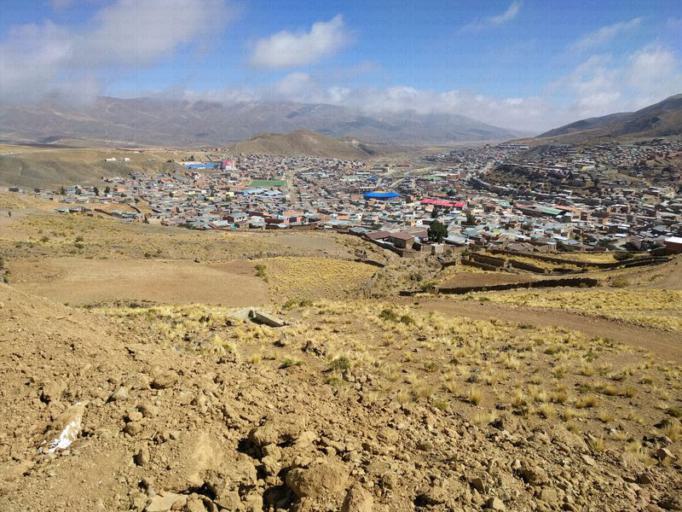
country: BO
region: Oruro
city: Huanuni
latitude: -18.2907
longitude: -66.8318
